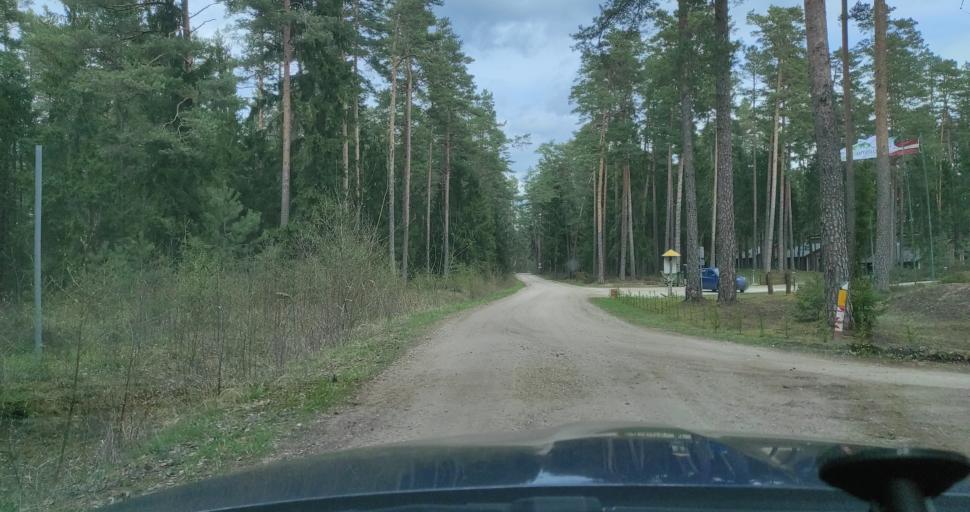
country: LV
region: Talsu Rajons
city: Stende
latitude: 57.2183
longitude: 22.2475
